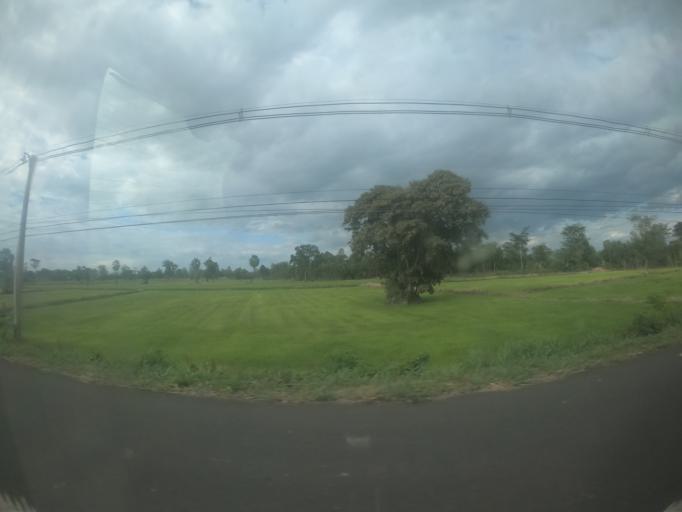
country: TH
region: Surin
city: Kap Choeng
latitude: 14.5339
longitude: 103.5275
